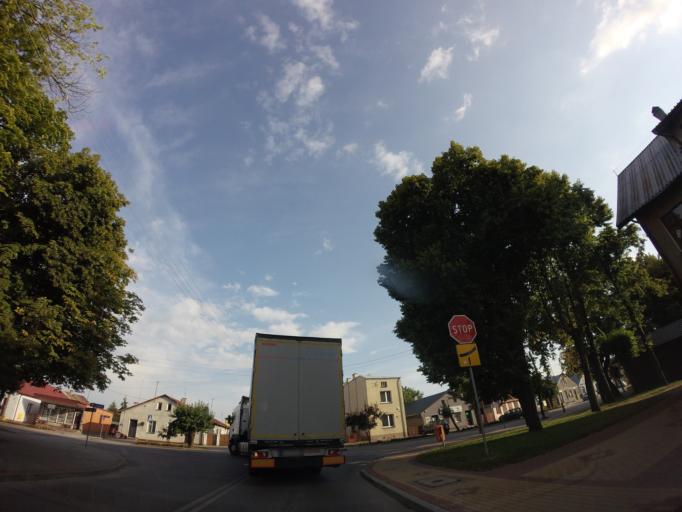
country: PL
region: Lublin Voivodeship
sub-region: Powiat lubartowski
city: Michow
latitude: 51.5236
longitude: 22.3143
